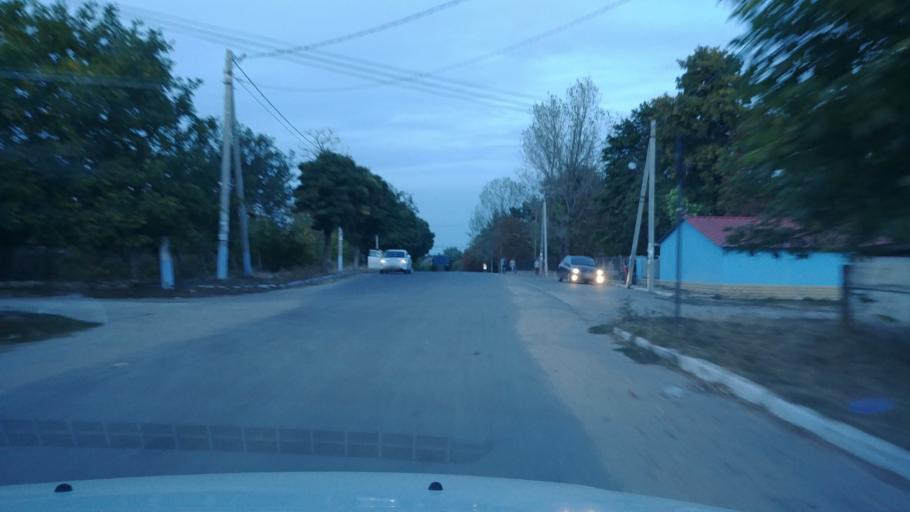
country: MD
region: Rezina
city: Saharna
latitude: 47.6730
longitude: 28.9546
